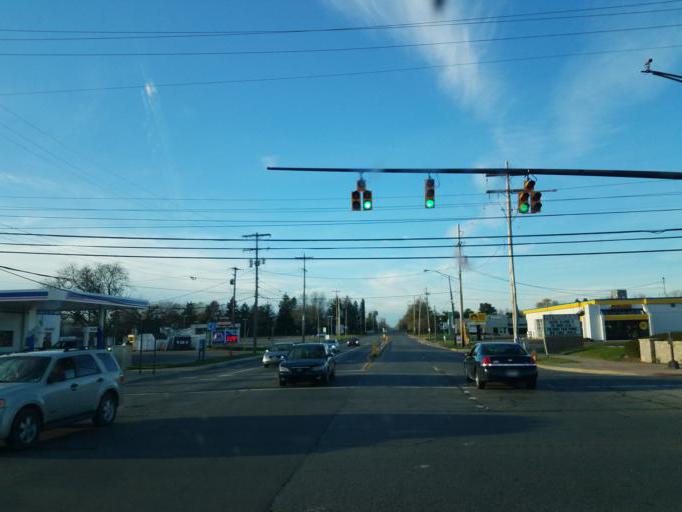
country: US
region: Ohio
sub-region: Franklin County
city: Minerva Park
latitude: 40.0604
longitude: -82.9774
